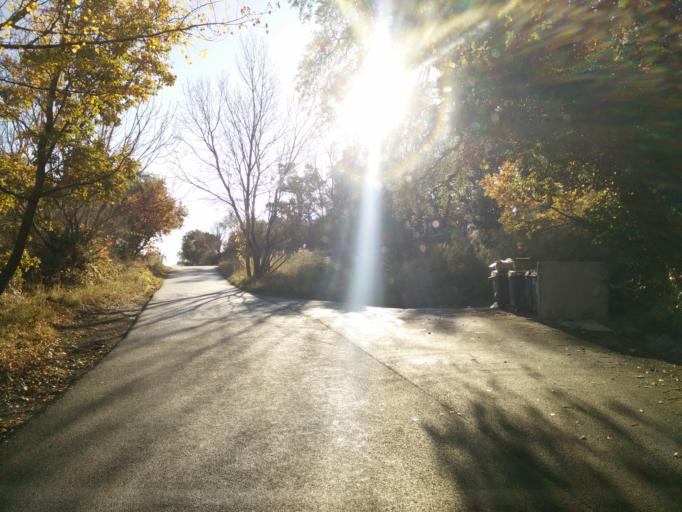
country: FR
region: Provence-Alpes-Cote d'Azur
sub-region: Departement du Var
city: La Garde-Freinet
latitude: 43.3002
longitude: 6.4908
